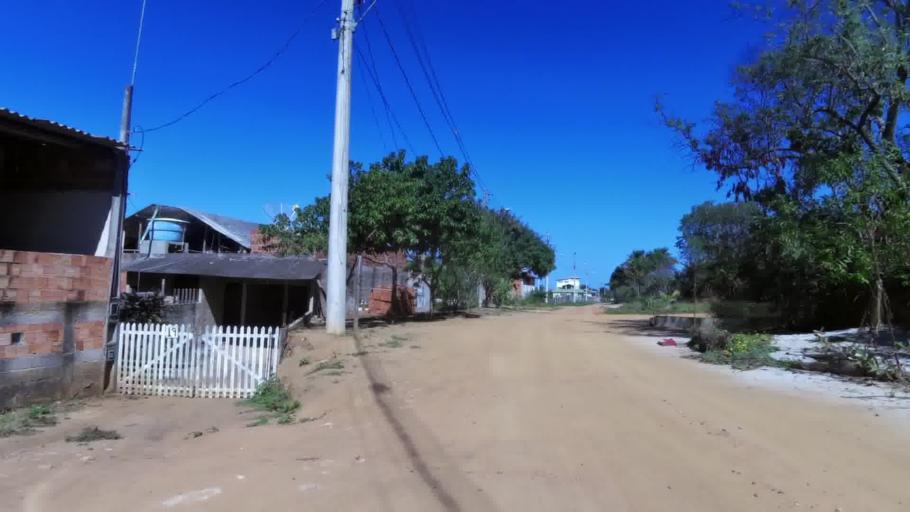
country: BR
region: Espirito Santo
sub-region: Guarapari
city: Guarapari
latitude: -20.7343
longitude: -40.5497
